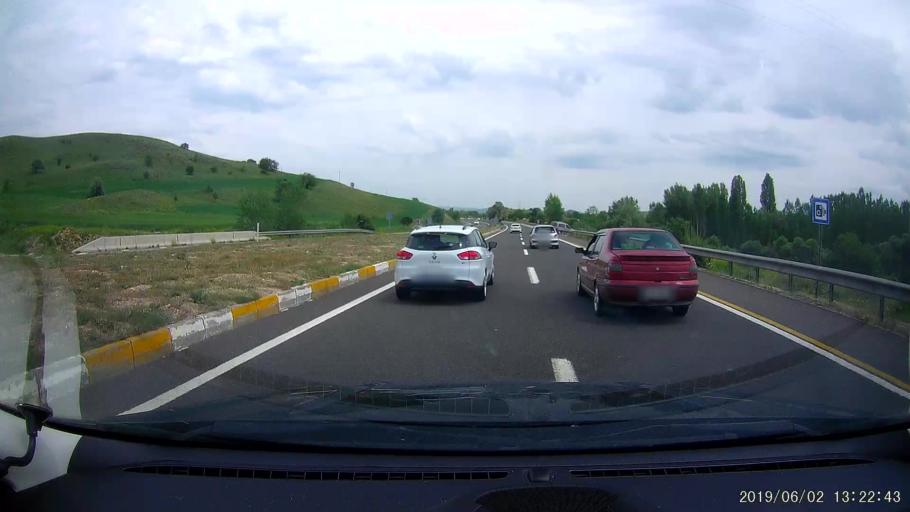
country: TR
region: Cankiri
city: Cerkes
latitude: 40.8258
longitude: 32.8035
